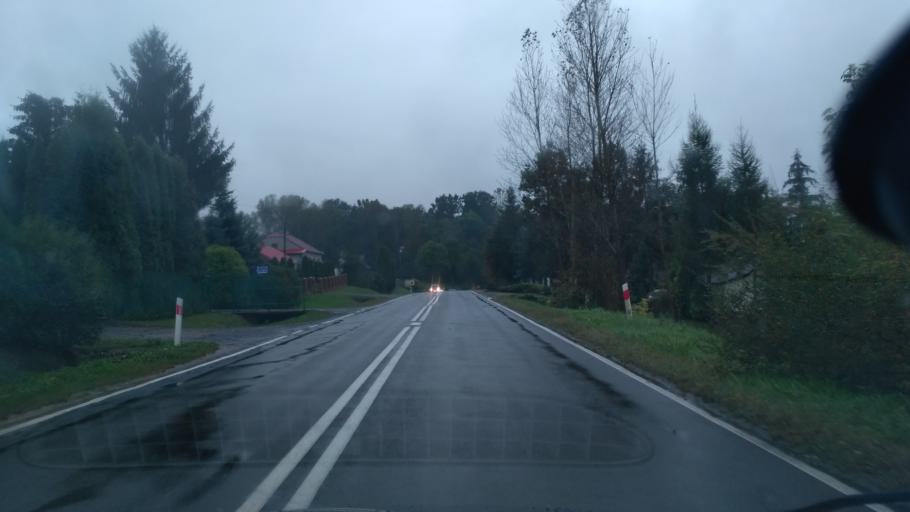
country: PL
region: Subcarpathian Voivodeship
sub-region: Powiat ropczycko-sedziszowski
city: Niedzwiada
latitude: 49.9926
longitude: 21.5640
